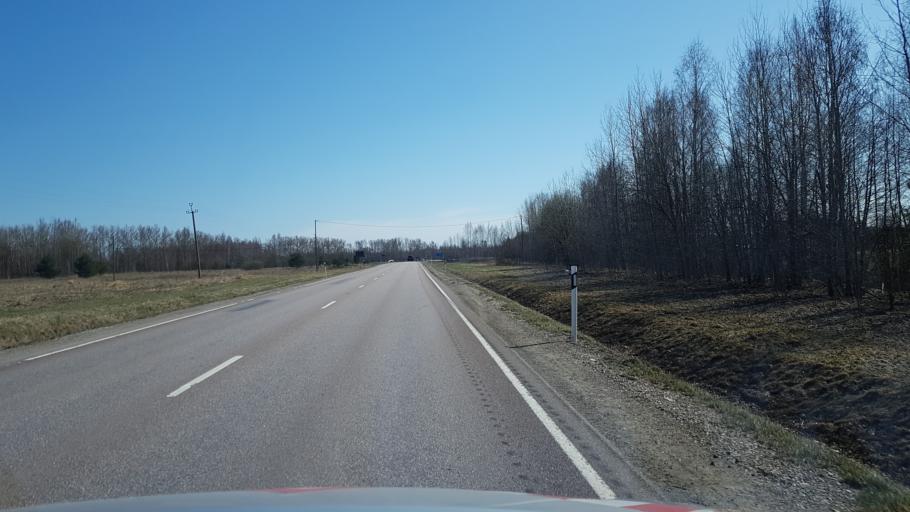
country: EE
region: Jogevamaa
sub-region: Mustvee linn
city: Mustvee
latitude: 58.7979
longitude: 26.9423
